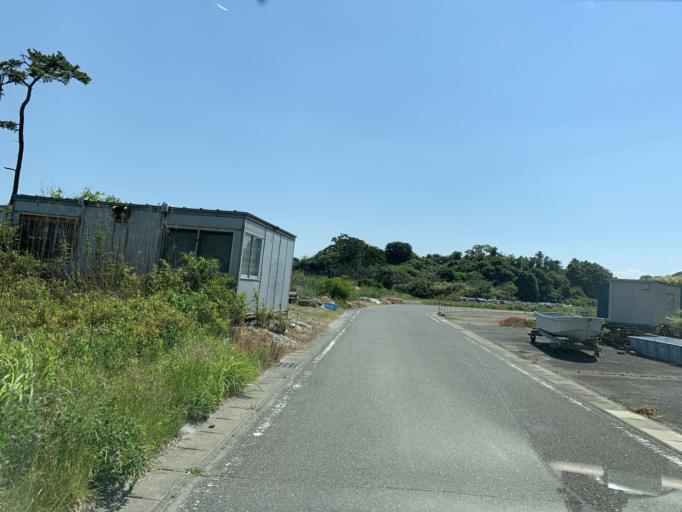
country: JP
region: Miyagi
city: Matsushima
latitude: 38.3275
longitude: 141.1597
